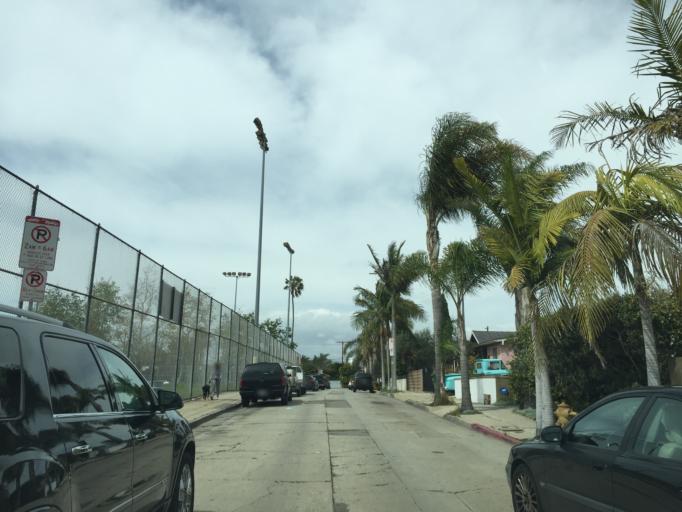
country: US
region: California
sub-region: Los Angeles County
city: Marina del Rey
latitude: 33.9955
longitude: -118.4640
